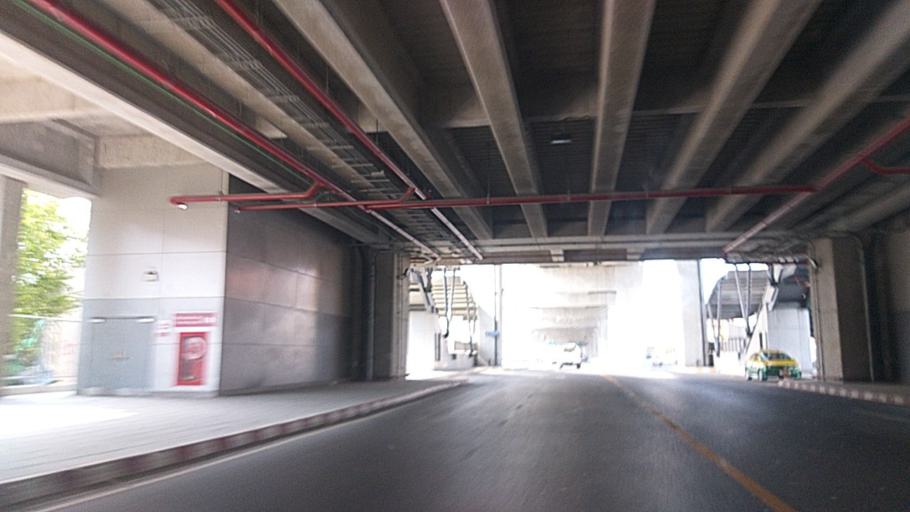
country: TH
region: Bangkok
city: Chatuchak
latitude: 13.8411
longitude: 100.5573
